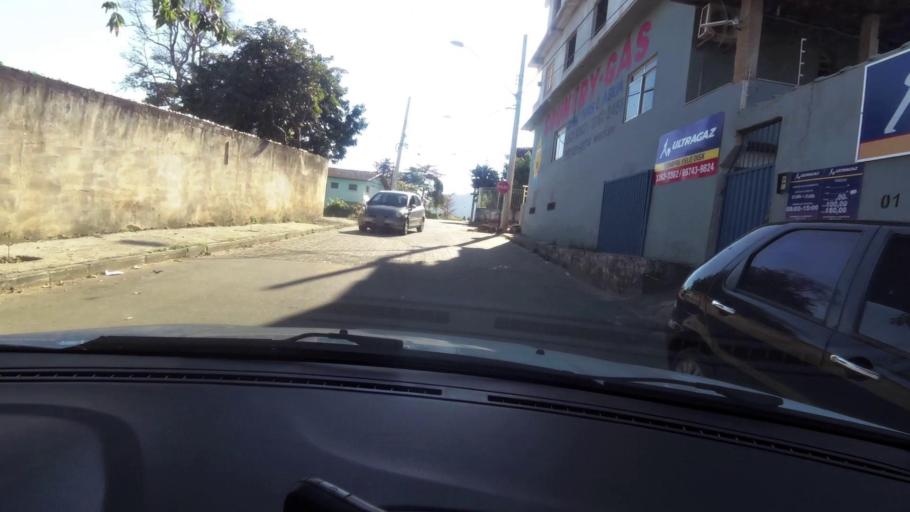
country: BR
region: Espirito Santo
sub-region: Guarapari
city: Guarapari
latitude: -20.6466
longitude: -40.5123
